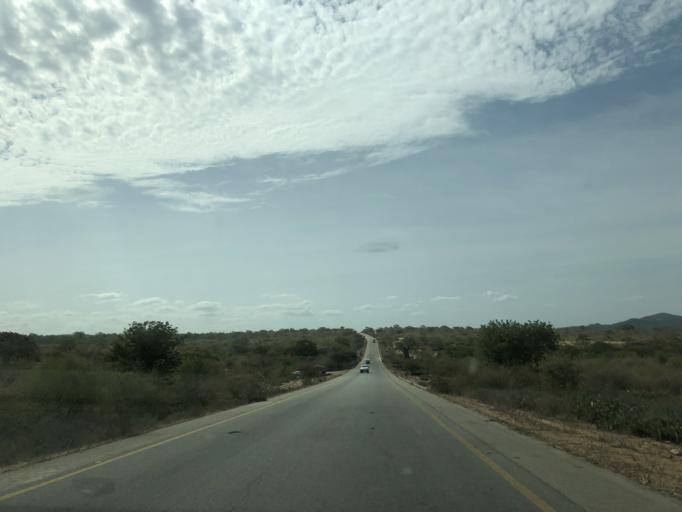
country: AO
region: Benguela
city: Benguela
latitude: -13.0167
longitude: 13.7209
